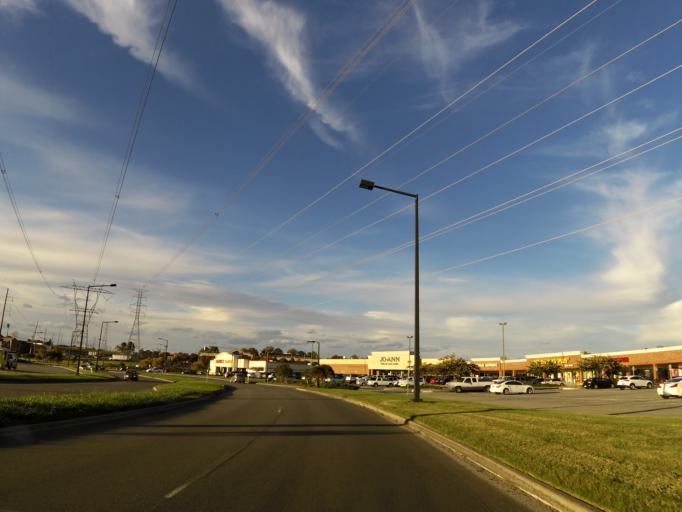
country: US
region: Tennessee
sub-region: Knox County
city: Farragut
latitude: 35.9145
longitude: -84.0819
